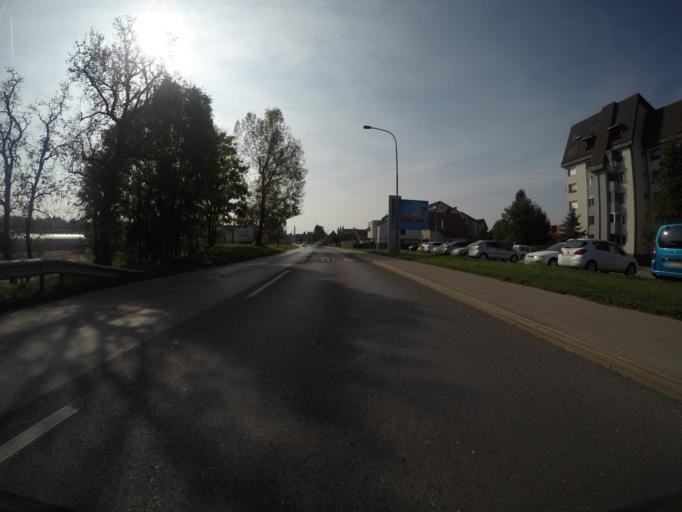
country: SI
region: Kamnik
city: Smarca
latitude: 46.2066
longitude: 14.5974
